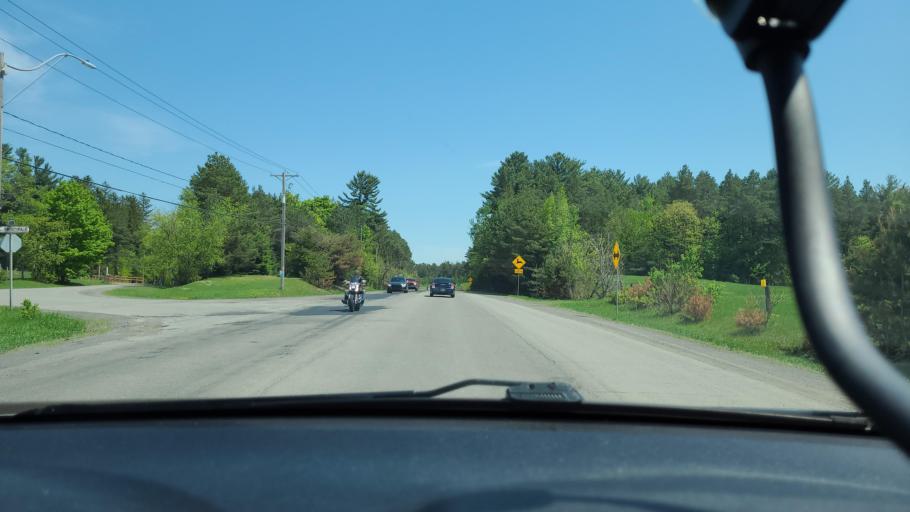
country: CA
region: Quebec
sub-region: Laurentides
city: Lachute
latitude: 45.6649
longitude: -74.2586
